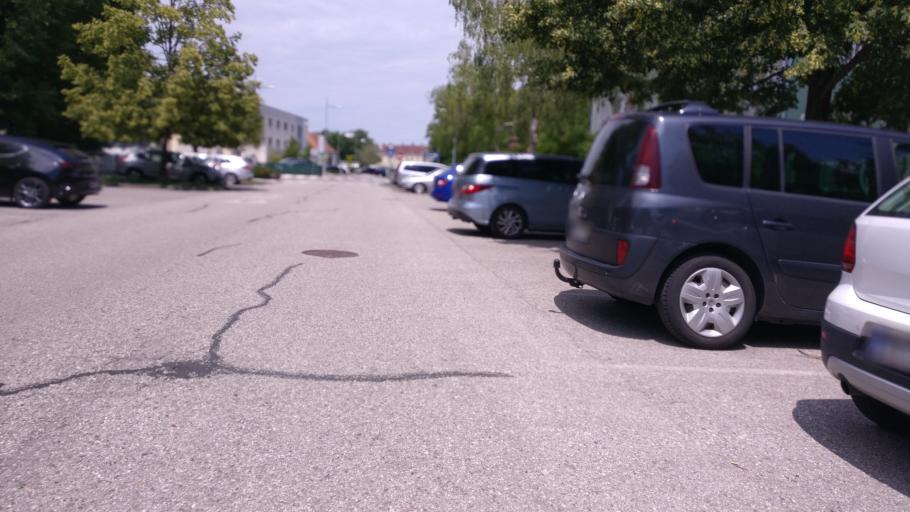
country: AT
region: Lower Austria
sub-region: Wiener Neustadt Stadt
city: Wiener Neustadt
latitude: 47.8201
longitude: 16.2463
